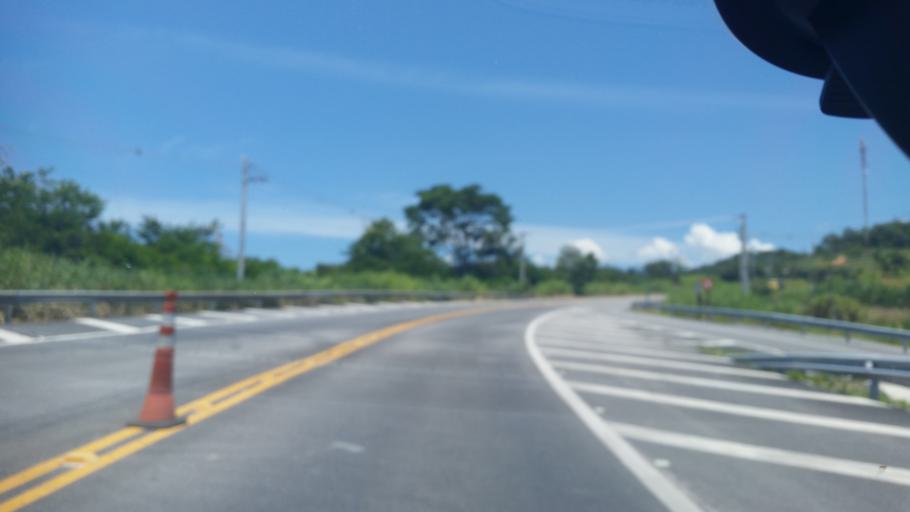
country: BR
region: Sao Paulo
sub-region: Taubate
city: Taubate
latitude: -23.0842
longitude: -45.5435
